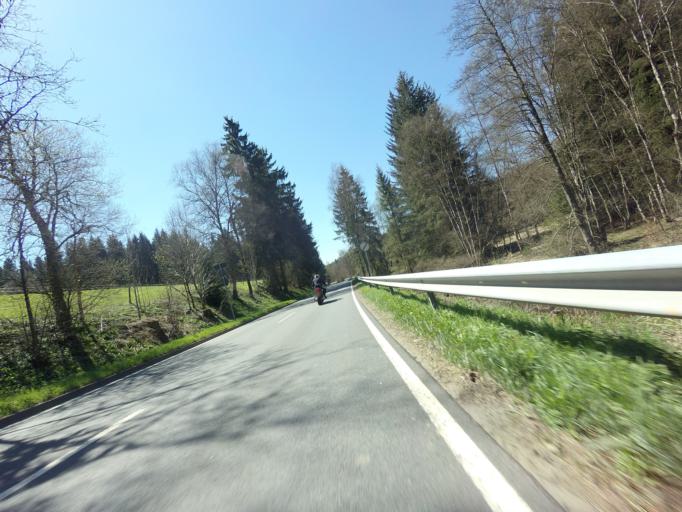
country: DE
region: North Rhine-Westphalia
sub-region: Regierungsbezirk Arnsberg
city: Erndtebruck
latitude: 51.0515
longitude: 8.2311
